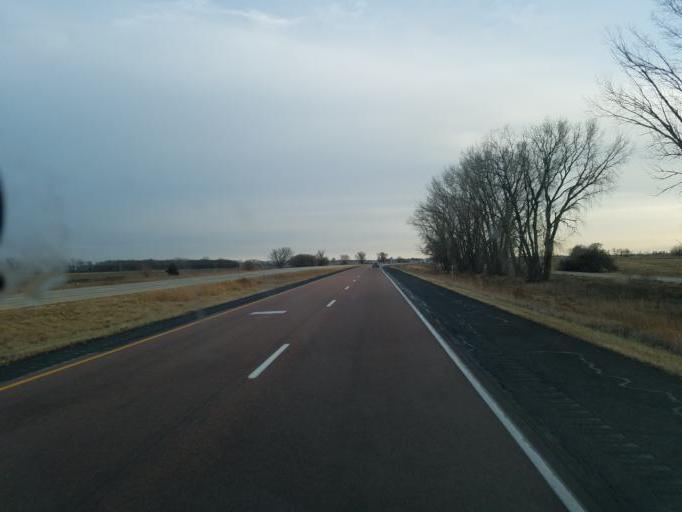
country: US
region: Iowa
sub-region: Monona County
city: Onawa
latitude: 41.9758
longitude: -96.1031
